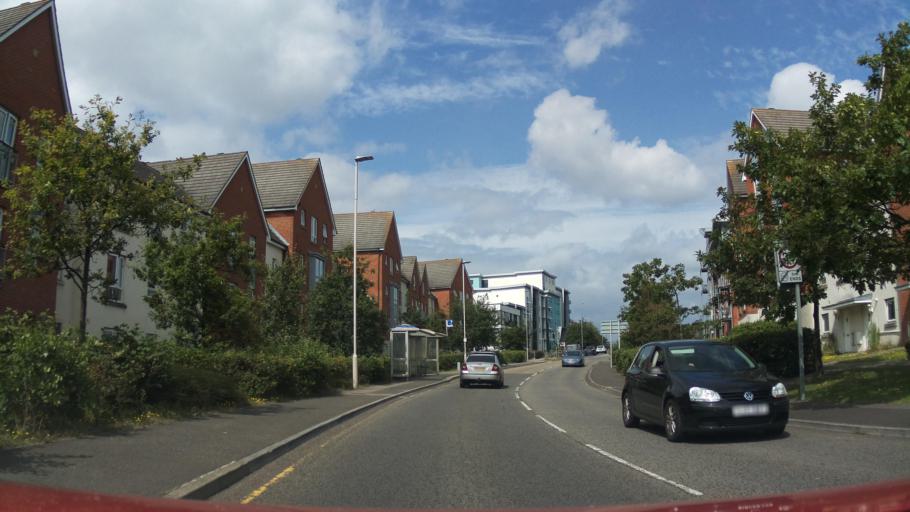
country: GB
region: England
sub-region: Poole
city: Poole
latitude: 50.7140
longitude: -1.9776
